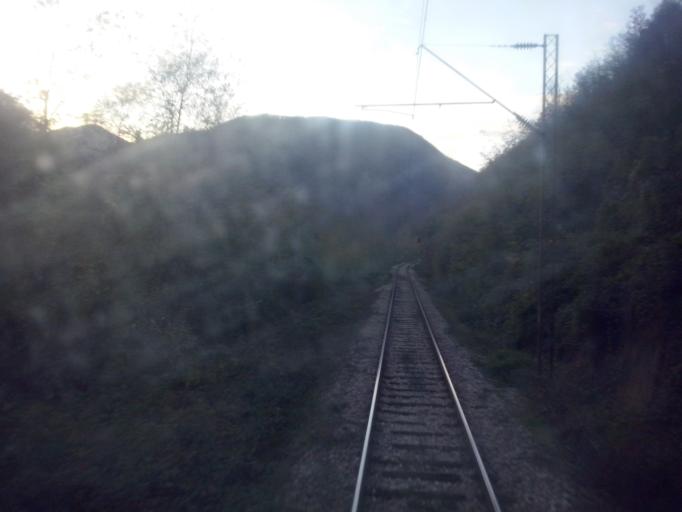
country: RS
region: Central Serbia
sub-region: Kolubarski Okrug
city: Valjevo
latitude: 44.1537
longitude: 19.8957
